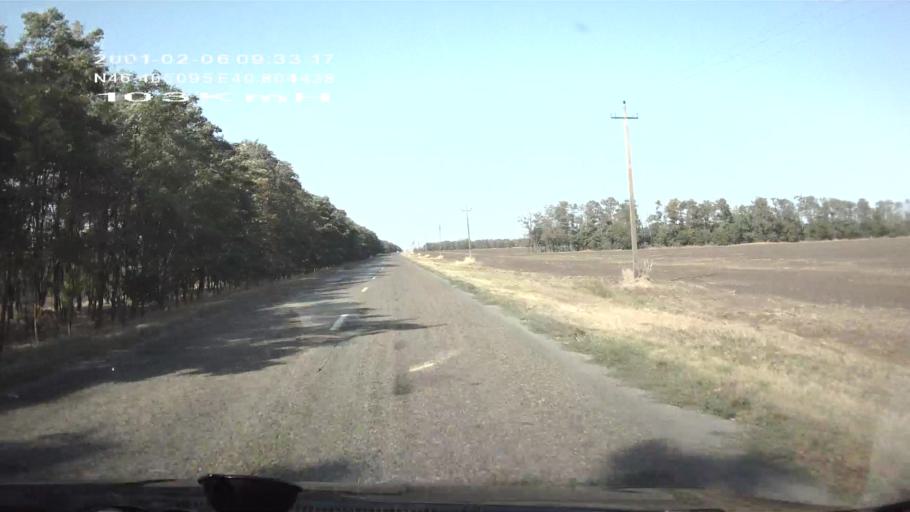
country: RU
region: Rostov
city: Yegorlykskaya
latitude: 46.4651
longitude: 40.8036
